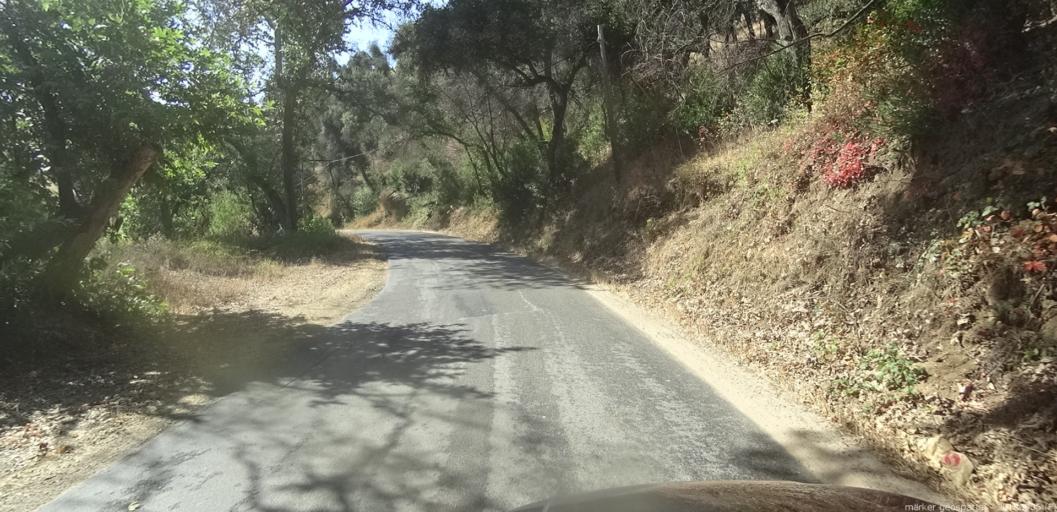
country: US
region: California
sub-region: Monterey County
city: Gonzales
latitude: 36.3865
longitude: -121.5963
